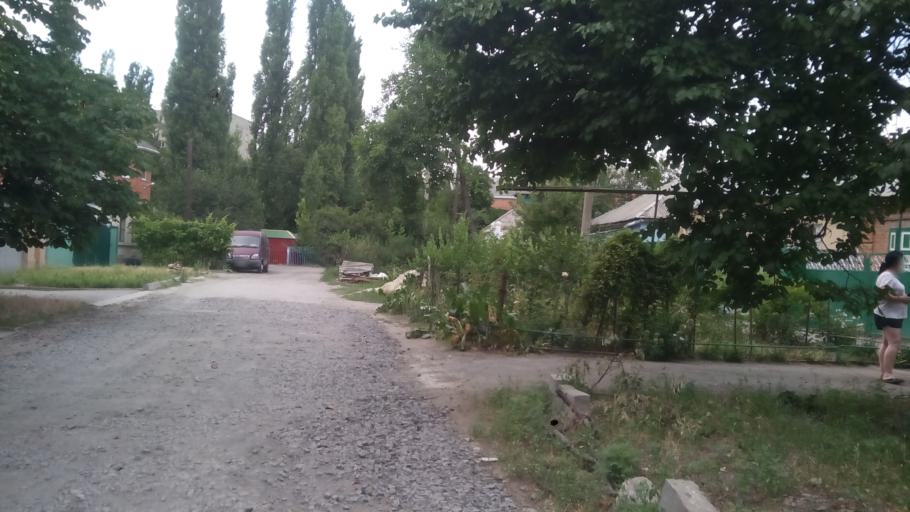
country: RU
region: Rostov
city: Rostov-na-Donu
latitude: 47.2285
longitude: 39.6353
